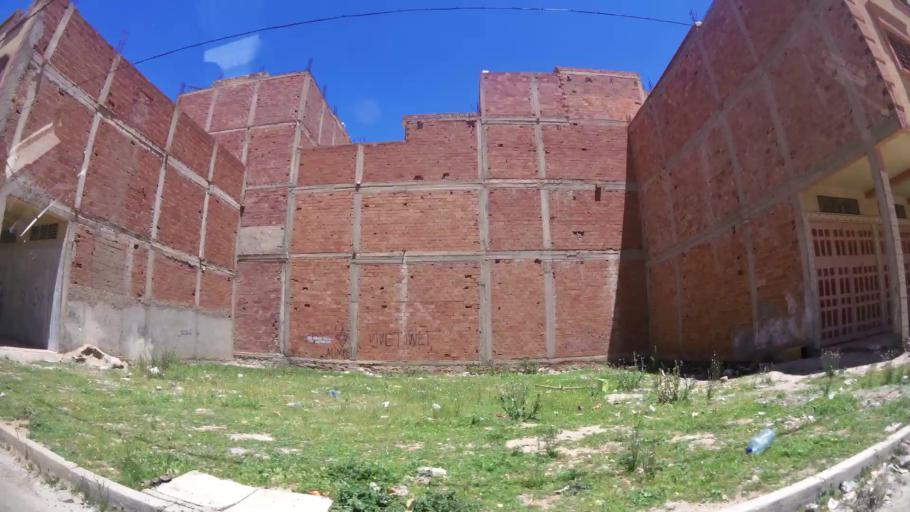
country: MA
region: Oriental
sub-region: Oujda-Angad
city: Oujda
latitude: 34.6774
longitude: -1.8721
